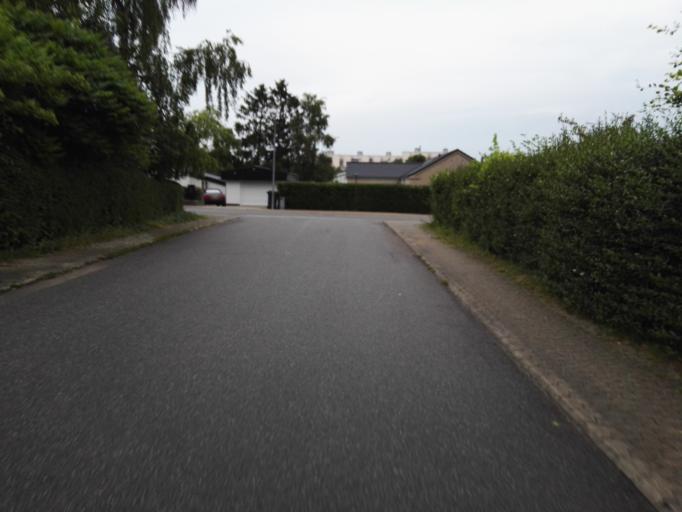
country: DK
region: Capital Region
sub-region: Egedal Kommune
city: Smorumnedre
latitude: 55.7481
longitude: 12.3114
